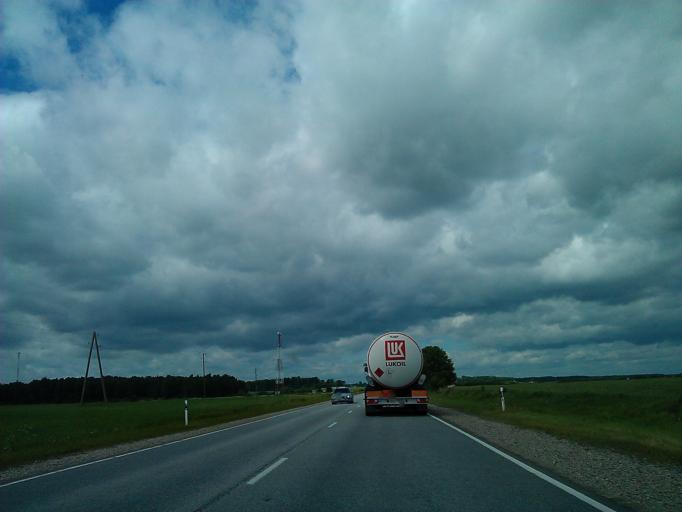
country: LV
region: Engure
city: Smarde
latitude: 56.9151
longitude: 23.3337
